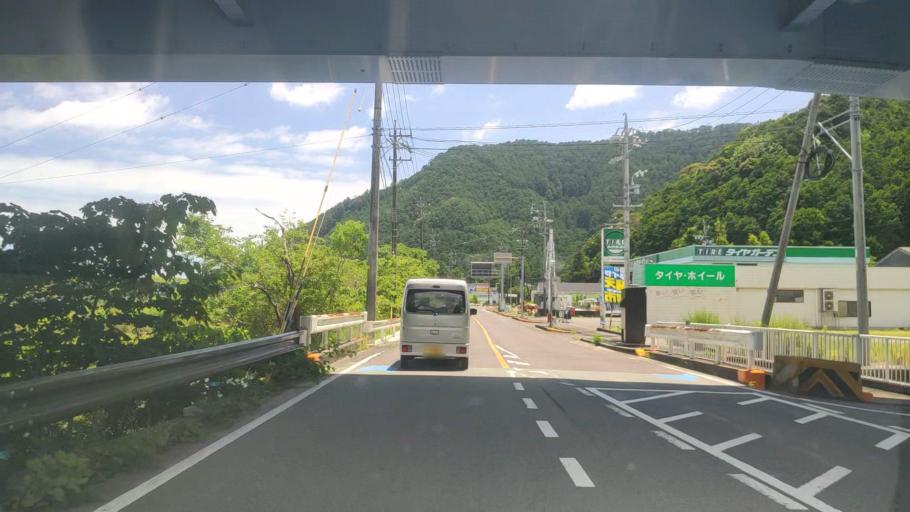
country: JP
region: Mie
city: Owase
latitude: 34.1190
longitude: 136.2193
